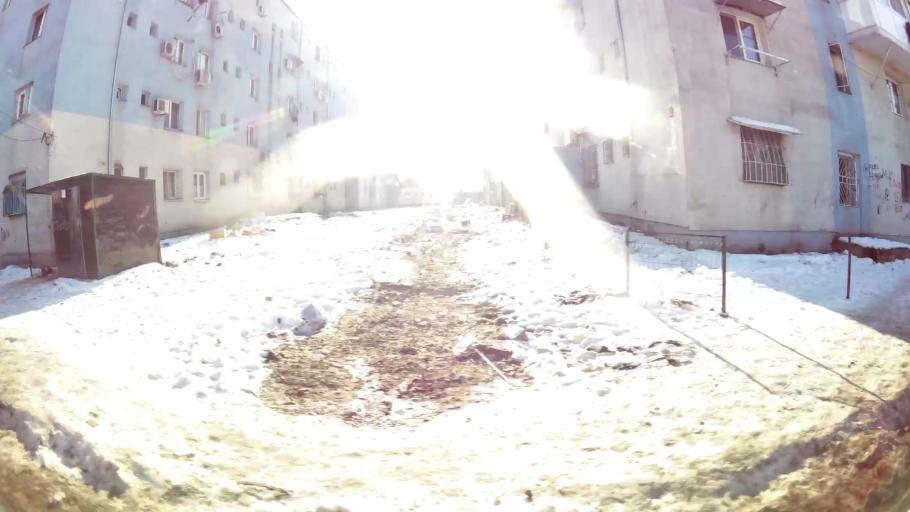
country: RO
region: Bucuresti
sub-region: Municipiul Bucuresti
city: Bucuresti
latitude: 44.4015
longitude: 26.0878
